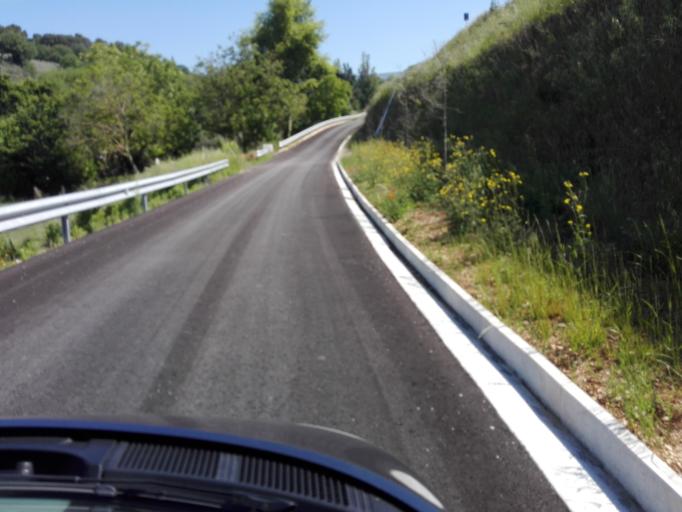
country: IT
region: Umbria
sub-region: Provincia di Perugia
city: Foligno
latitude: 42.9553
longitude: 12.7328
